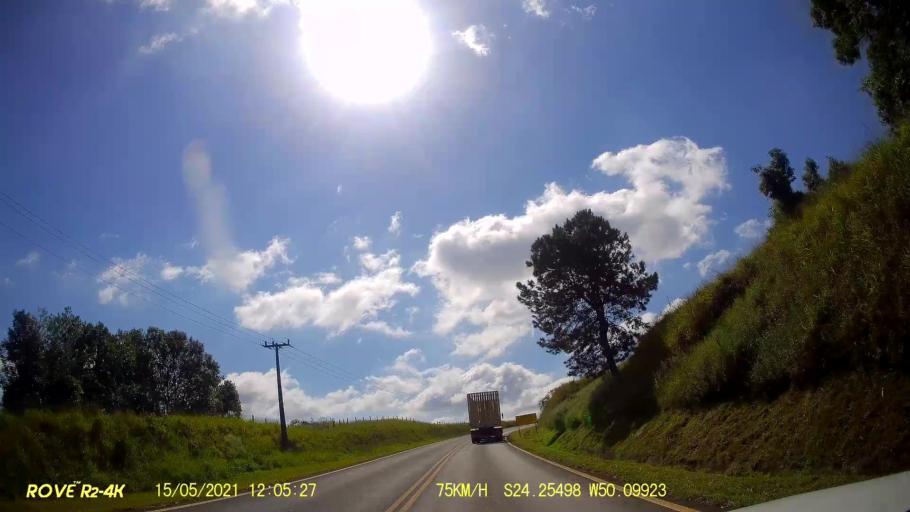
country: BR
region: Parana
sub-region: Pirai Do Sul
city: Pirai do Sul
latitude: -24.2550
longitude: -50.0992
